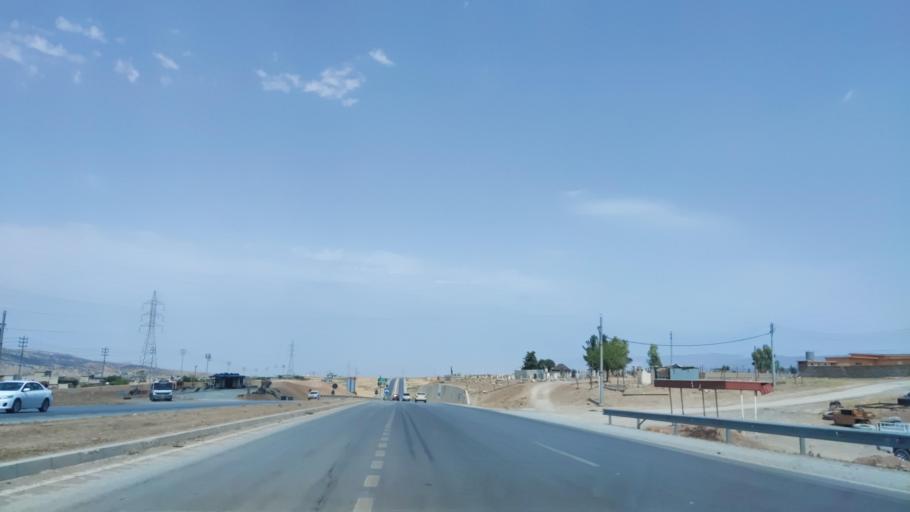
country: IQ
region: Arbil
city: Shaqlawah
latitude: 36.5068
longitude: 44.3495
